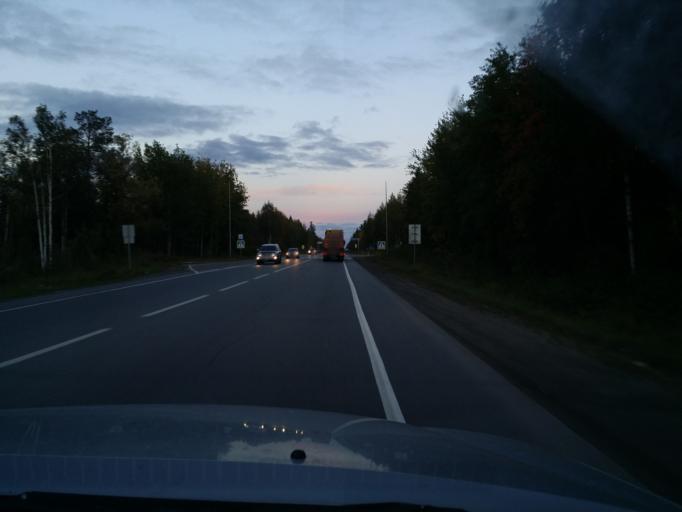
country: RU
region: Khanty-Mansiyskiy Avtonomnyy Okrug
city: Megion
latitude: 61.0599
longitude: 76.2861
